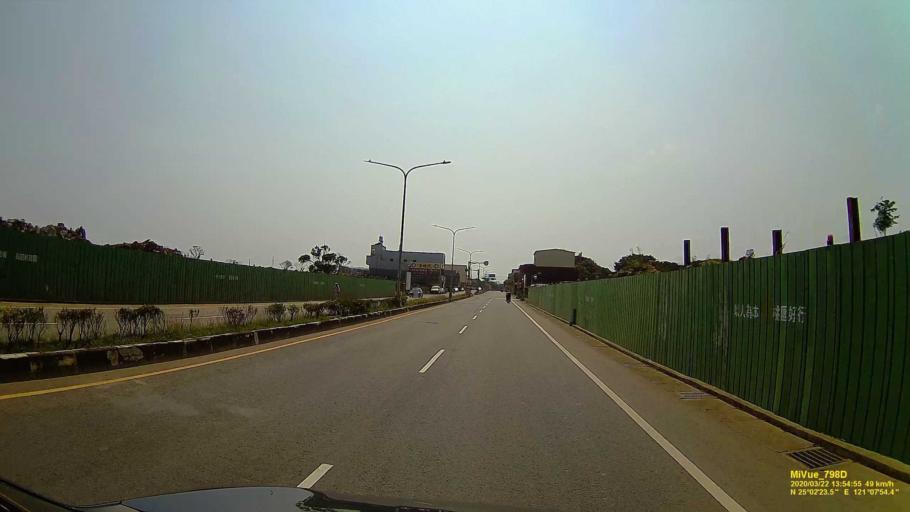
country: TW
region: Taiwan
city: Taoyuan City
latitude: 25.0398
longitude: 121.1316
